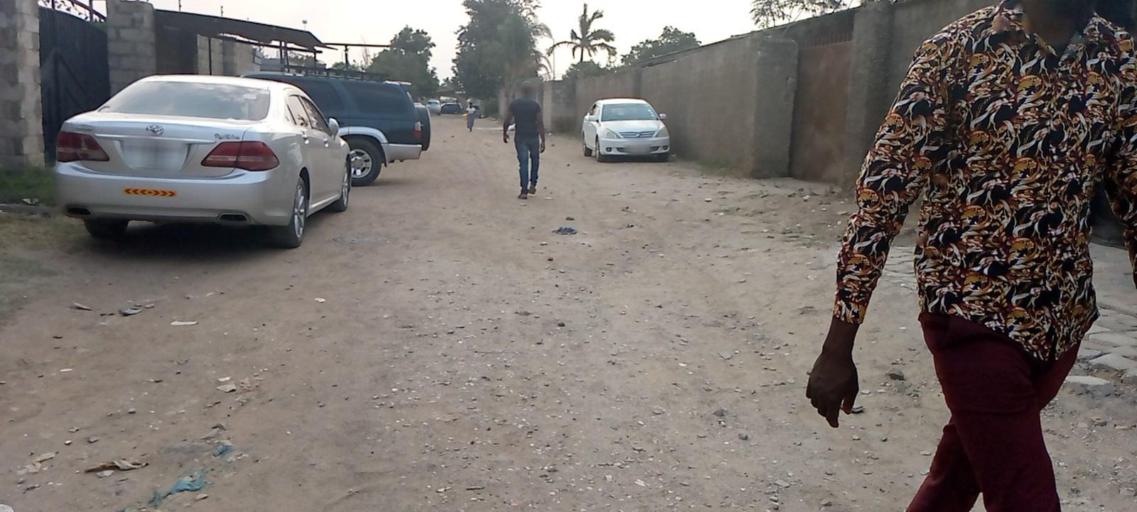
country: ZM
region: Lusaka
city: Lusaka
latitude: -15.4036
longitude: 28.3460
